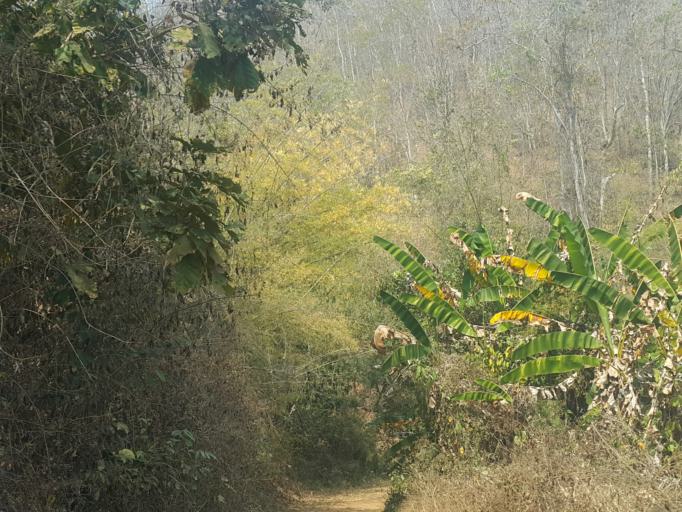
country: TH
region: Chiang Mai
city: Hang Dong
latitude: 18.7524
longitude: 98.8270
